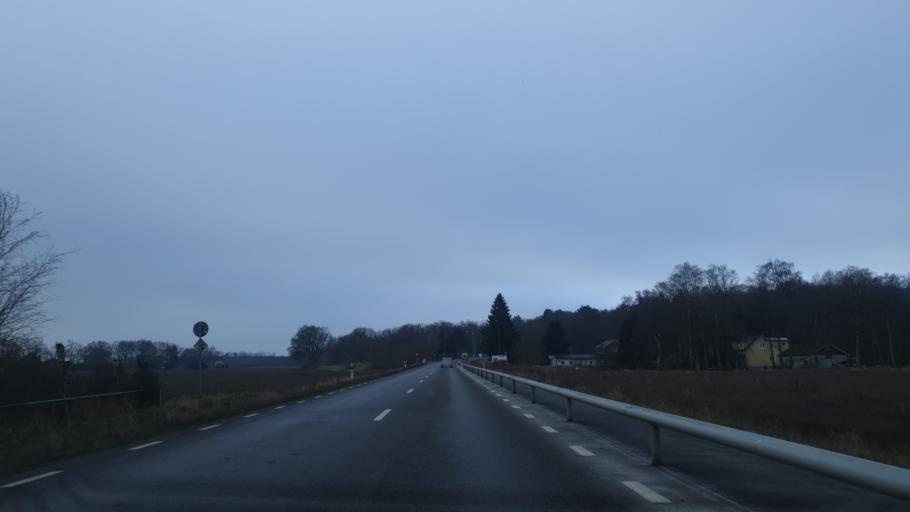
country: SE
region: Blekinge
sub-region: Solvesborgs Kommun
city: Soelvesborg
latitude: 56.0967
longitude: 14.6606
